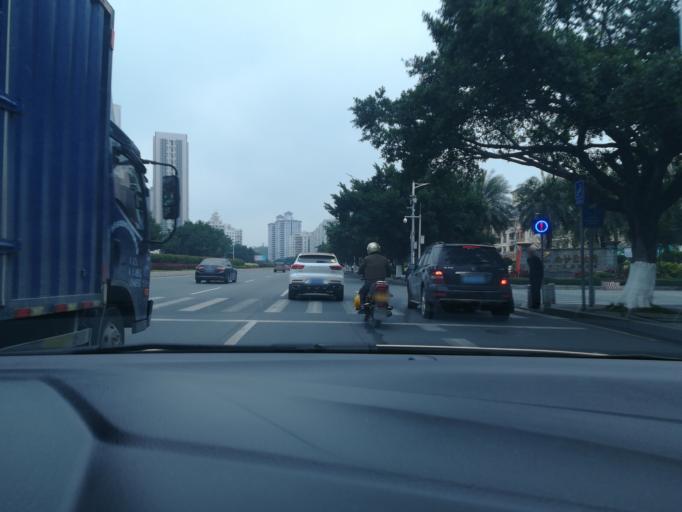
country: CN
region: Guangdong
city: Nansha
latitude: 22.8018
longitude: 113.5503
